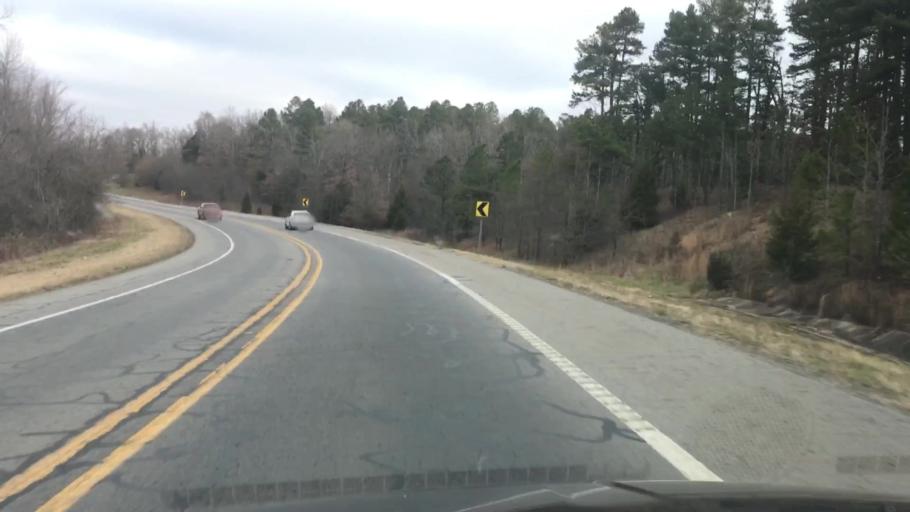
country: US
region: Arkansas
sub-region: Scott County
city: Waldron
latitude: 34.8233
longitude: -94.0362
